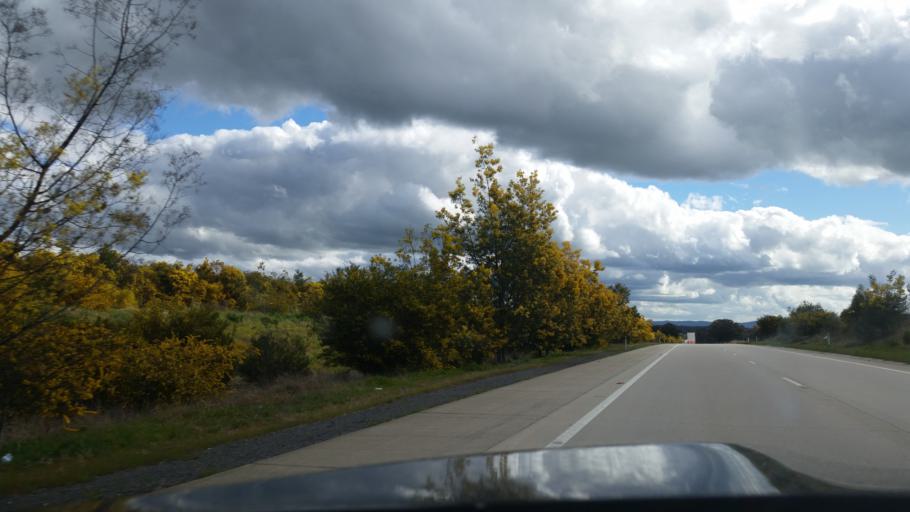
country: AU
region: New South Wales
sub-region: Greater Hume Shire
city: Jindera
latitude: -35.9244
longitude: 147.0521
